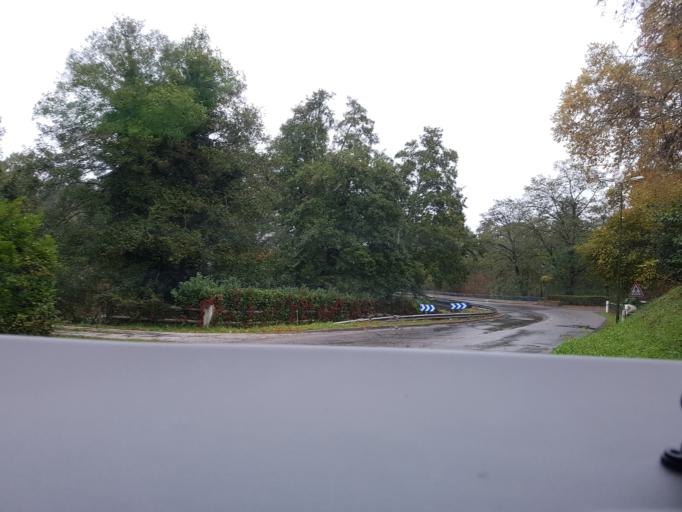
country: FR
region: Aquitaine
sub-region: Departement de la Gironde
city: Saint-Symphorien
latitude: 44.3222
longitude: -0.5860
